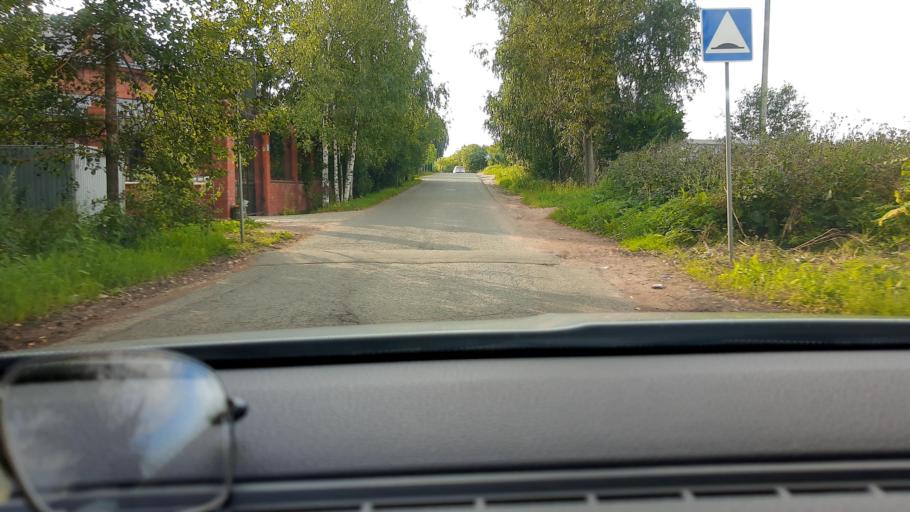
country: RU
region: Moskovskaya
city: Nekrasovskiy
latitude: 56.1011
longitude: 37.5296
